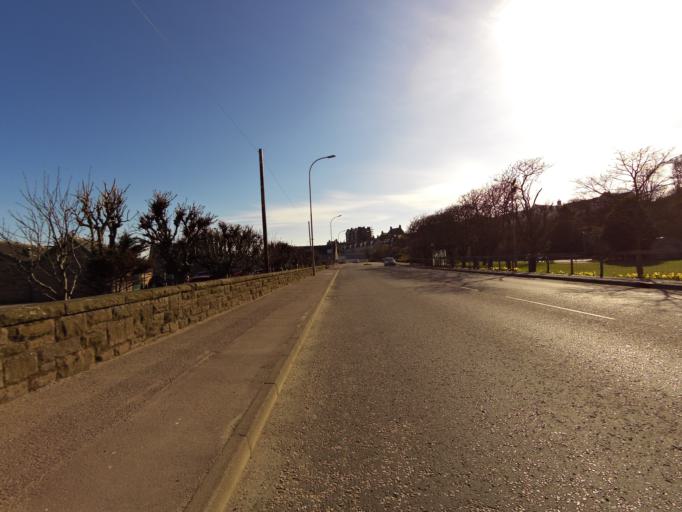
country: GB
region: Scotland
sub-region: Aberdeenshire
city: Stonehaven
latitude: 56.9687
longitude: -2.2081
